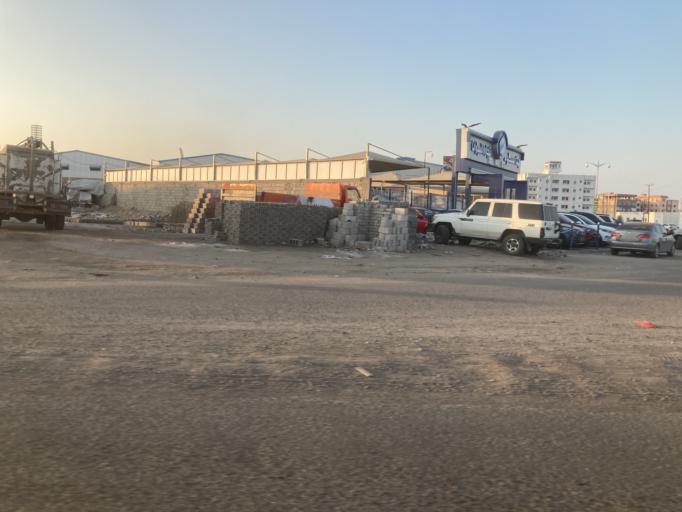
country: YE
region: Aden
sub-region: Ash Shaikh Outhman
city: Ash Shaykh `Uthman
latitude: 12.8628
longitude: 45.0169
